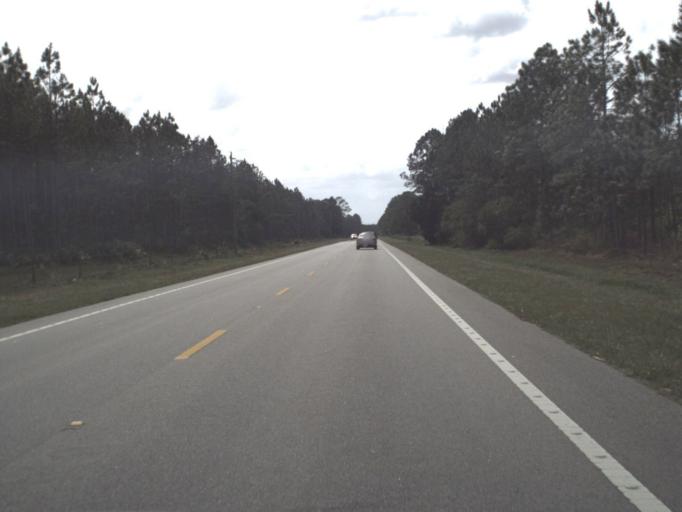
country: US
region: Florida
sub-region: Putnam County
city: Crescent City
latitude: 29.4808
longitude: -81.4327
